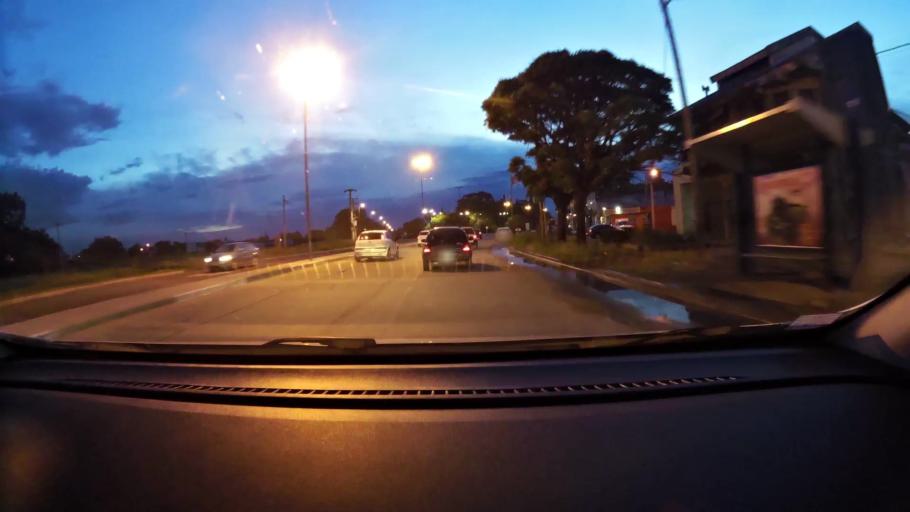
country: AR
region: Buenos Aires
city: San Nicolas de los Arroyos
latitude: -33.3505
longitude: -60.2365
